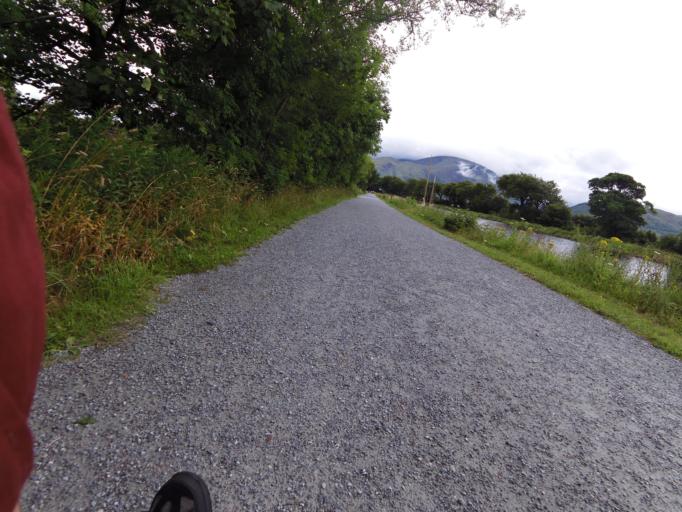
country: GB
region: Scotland
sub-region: Highland
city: Fort William
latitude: 56.8418
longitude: -5.1139
